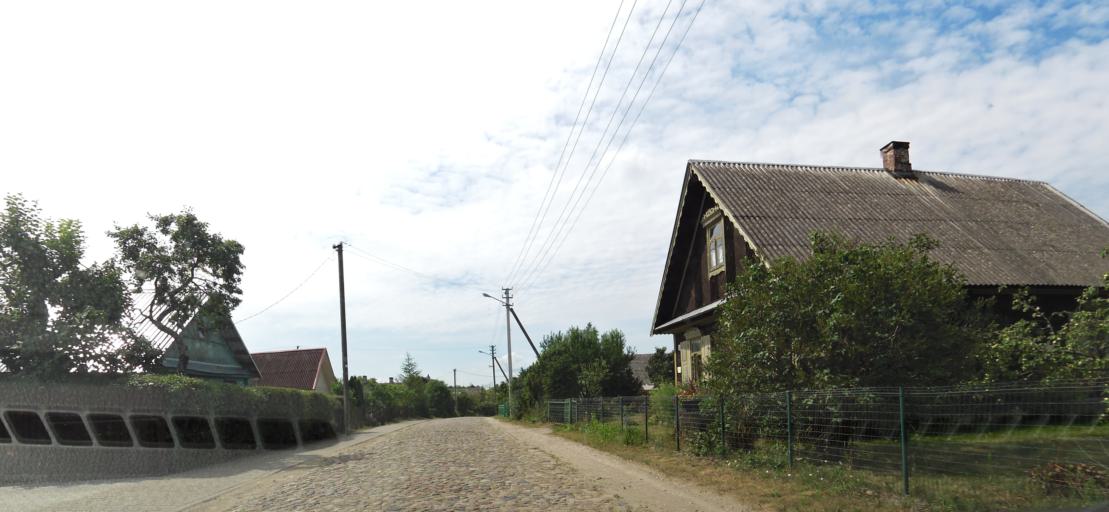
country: LT
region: Vilnius County
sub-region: Trakai
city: Rudiskes
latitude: 54.3551
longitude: 24.8365
